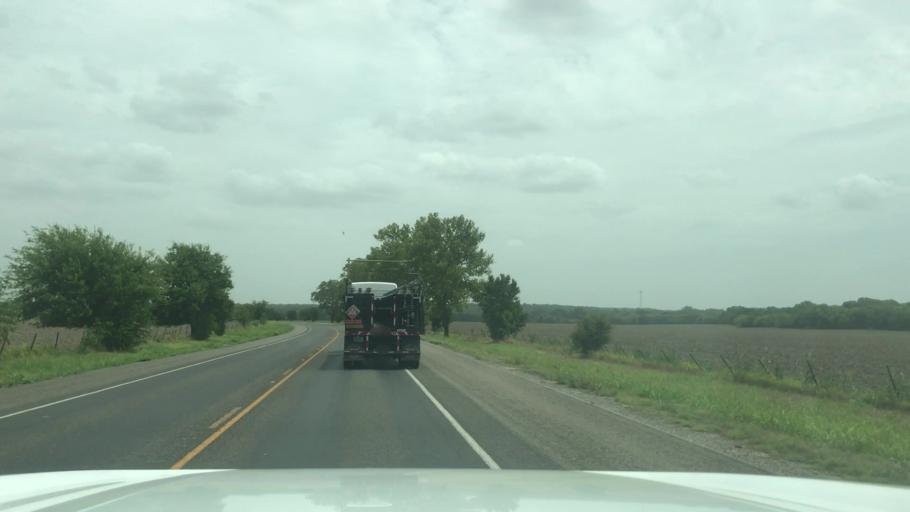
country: US
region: Texas
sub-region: Bosque County
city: Valley Mills
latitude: 31.6673
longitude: -97.4970
